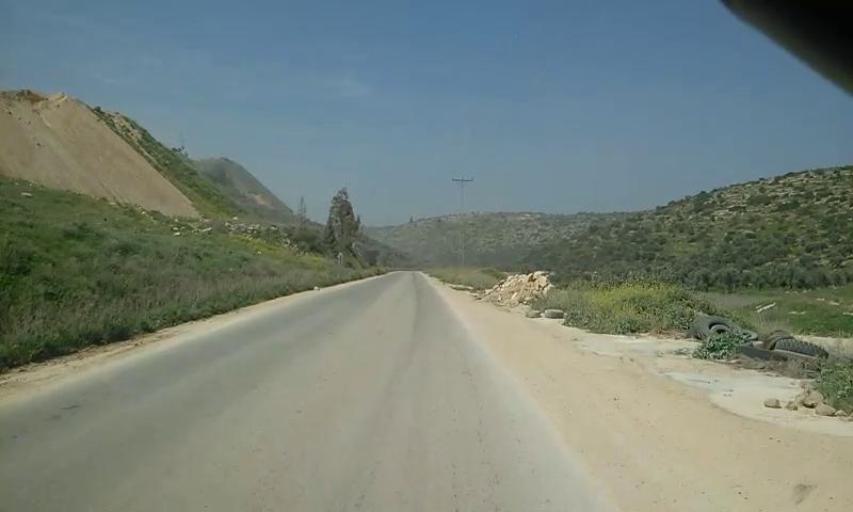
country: PS
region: West Bank
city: Az Zababidah
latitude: 32.4046
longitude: 35.3154
